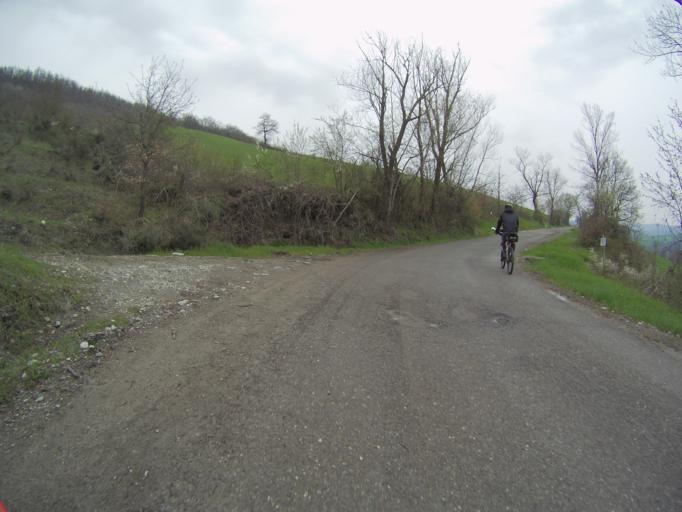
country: IT
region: Emilia-Romagna
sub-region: Provincia di Reggio Emilia
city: Casina
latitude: 44.5366
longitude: 10.4556
